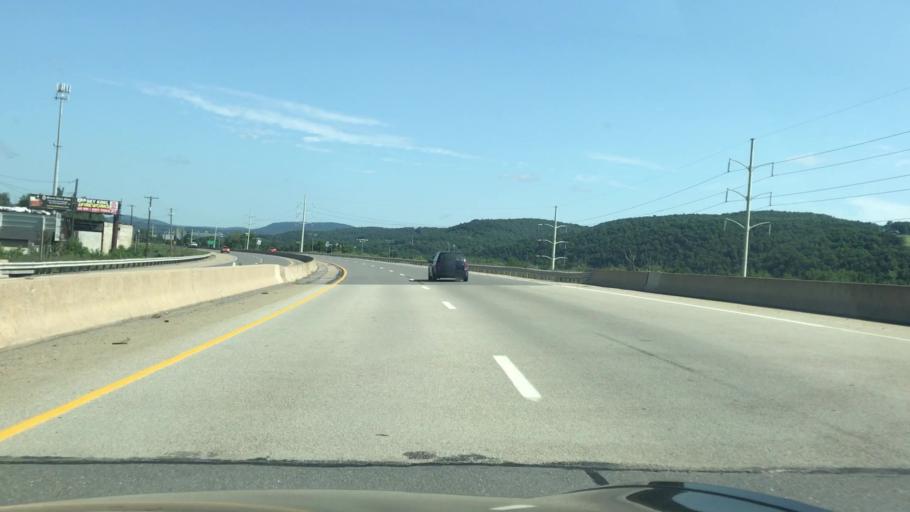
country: US
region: Pennsylvania
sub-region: Lycoming County
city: Garden View
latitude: 41.2544
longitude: -77.0455
